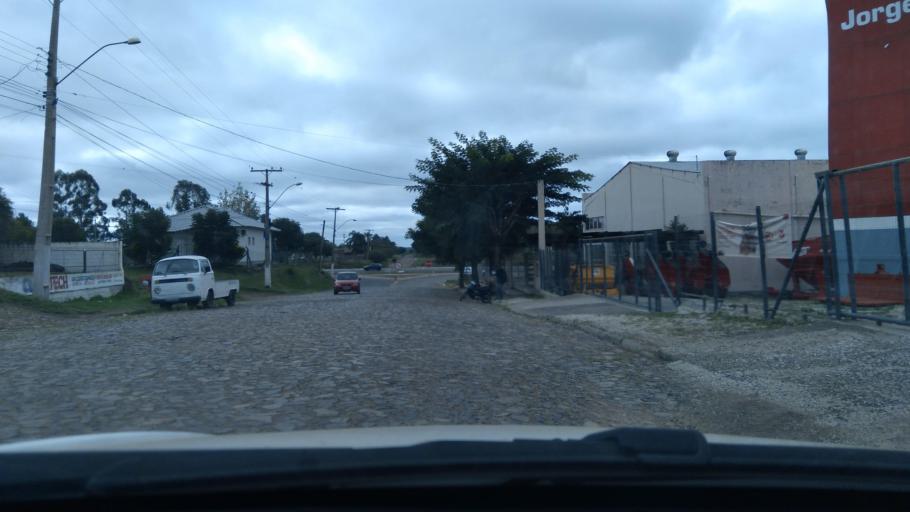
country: BR
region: Rio Grande do Sul
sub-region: Dom Pedrito
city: Dom Pedrito
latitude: -30.9645
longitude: -54.6721
